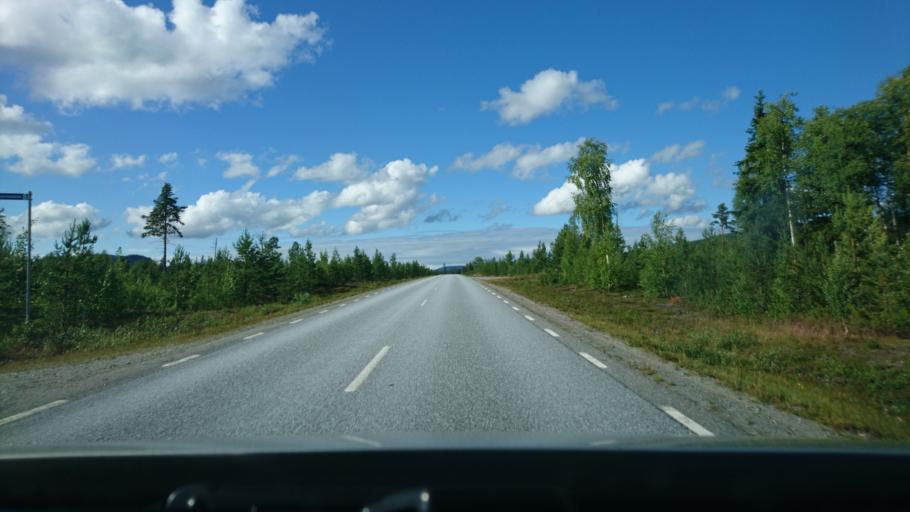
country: SE
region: Vaesterbotten
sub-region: Asele Kommun
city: Asele
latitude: 64.2293
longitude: 17.3008
